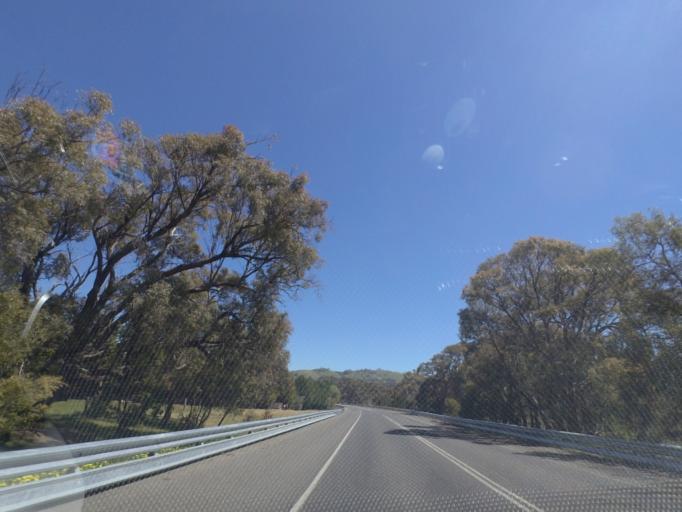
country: AU
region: Victoria
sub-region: Hume
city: Sunbury
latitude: -37.3000
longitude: 144.8255
